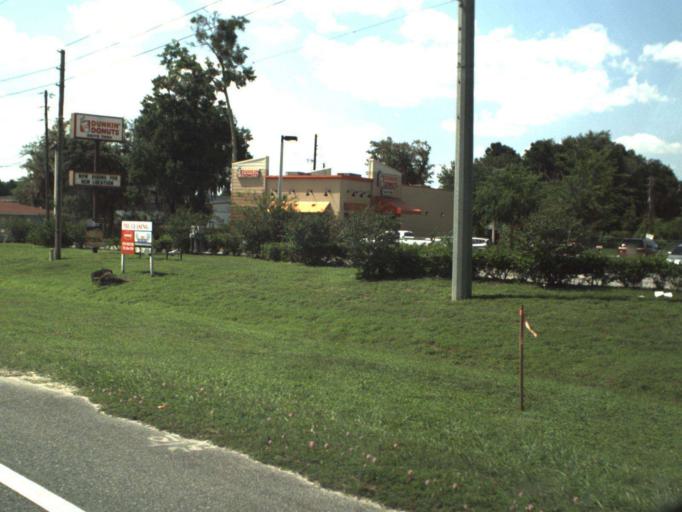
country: US
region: Florida
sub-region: Marion County
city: Silver Springs Shores
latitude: 29.1412
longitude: -82.0583
